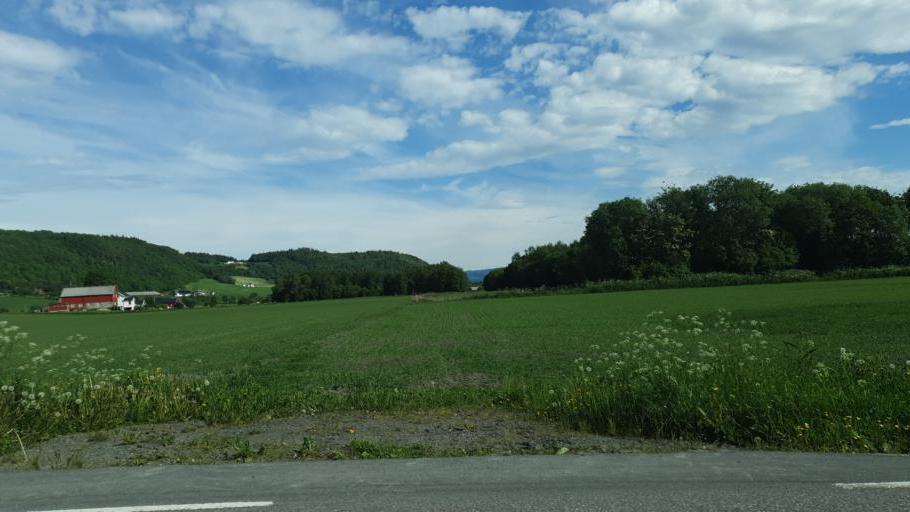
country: NO
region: Sor-Trondelag
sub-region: Rissa
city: Rissa
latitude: 63.5056
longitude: 10.0119
